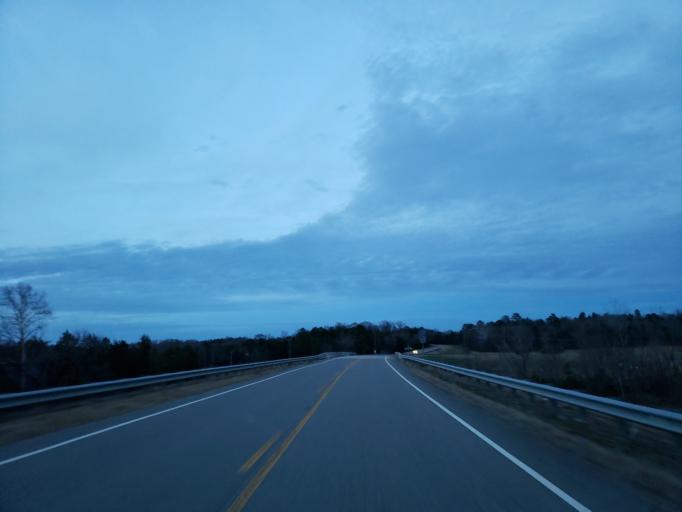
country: US
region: Alabama
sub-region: Greene County
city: Eutaw
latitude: 32.8579
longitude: -88.0999
